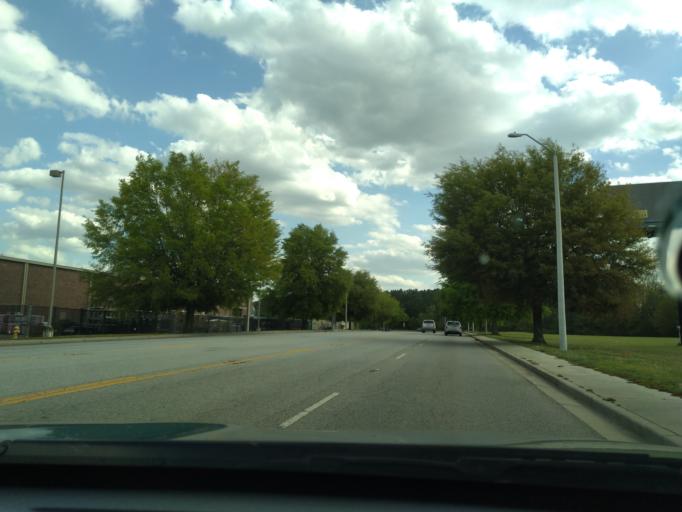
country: US
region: South Carolina
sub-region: Florence County
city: Florence
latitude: 34.1602
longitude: -79.7599
